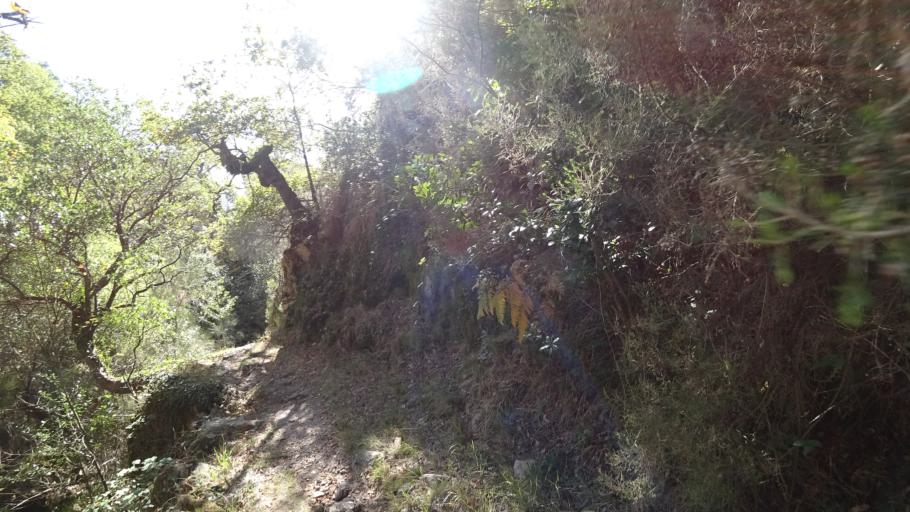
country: PT
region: Braga
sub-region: Vieira do Minho
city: Real
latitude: 41.7605
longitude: -8.1494
